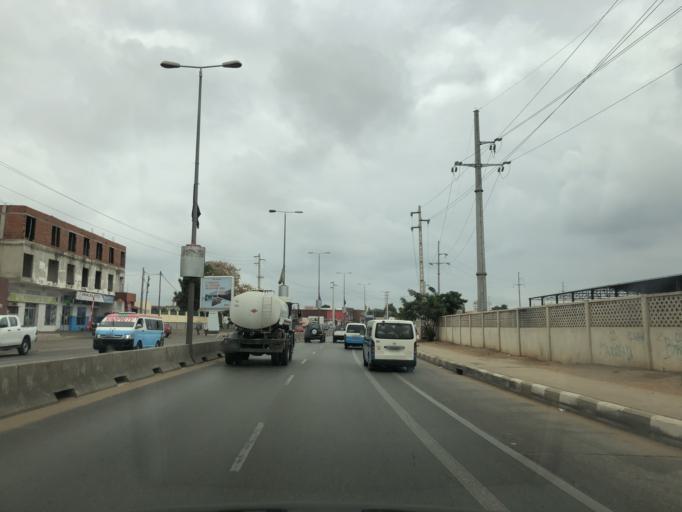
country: AO
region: Luanda
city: Luanda
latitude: -8.8946
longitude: 13.1933
